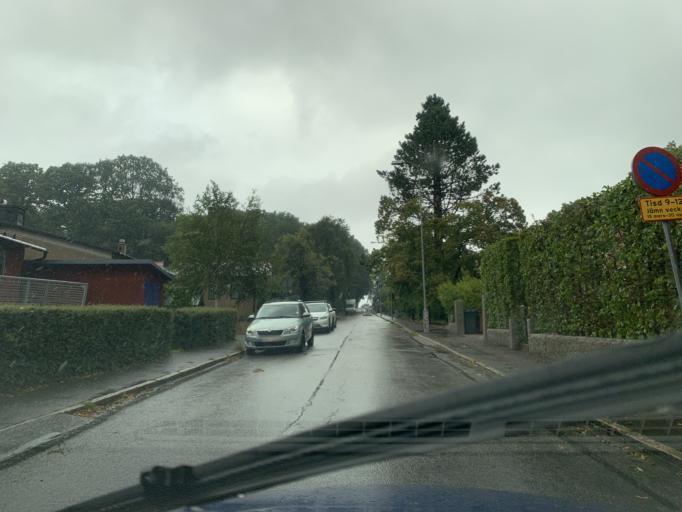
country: SE
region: Vaestra Goetaland
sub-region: Goteborg
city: Goeteborg
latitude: 57.7058
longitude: 12.0148
